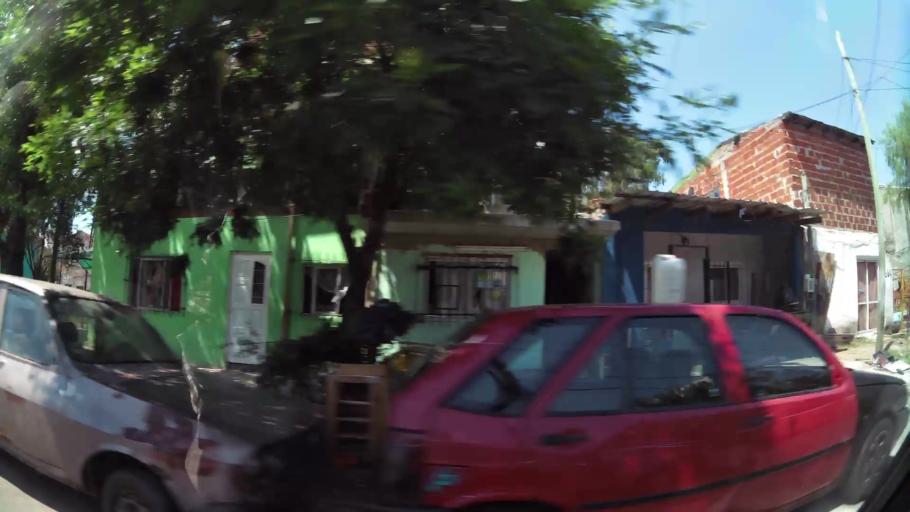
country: AR
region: Buenos Aires
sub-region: Partido de Tigre
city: Tigre
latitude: -34.4601
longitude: -58.5819
